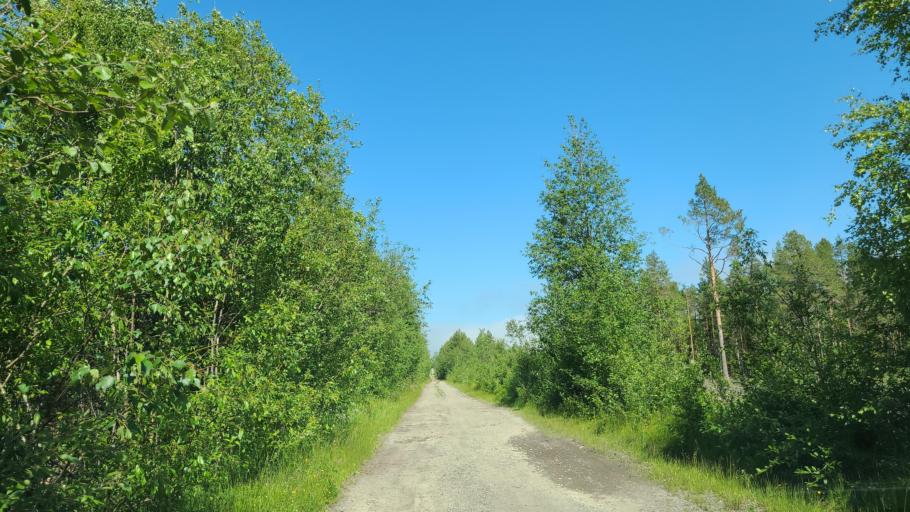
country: SE
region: Vaesternorrland
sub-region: OErnskoeldsviks Kommun
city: Husum
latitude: 63.4264
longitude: 19.2263
